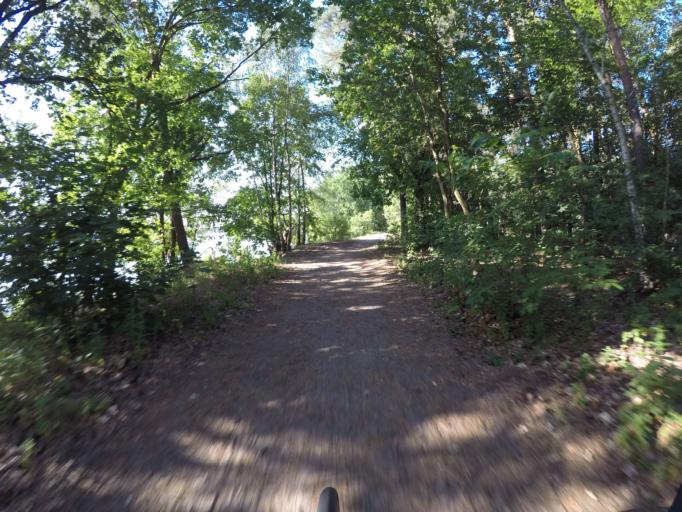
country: DE
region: Brandenburg
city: Zeuthen
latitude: 52.4062
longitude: 13.6236
